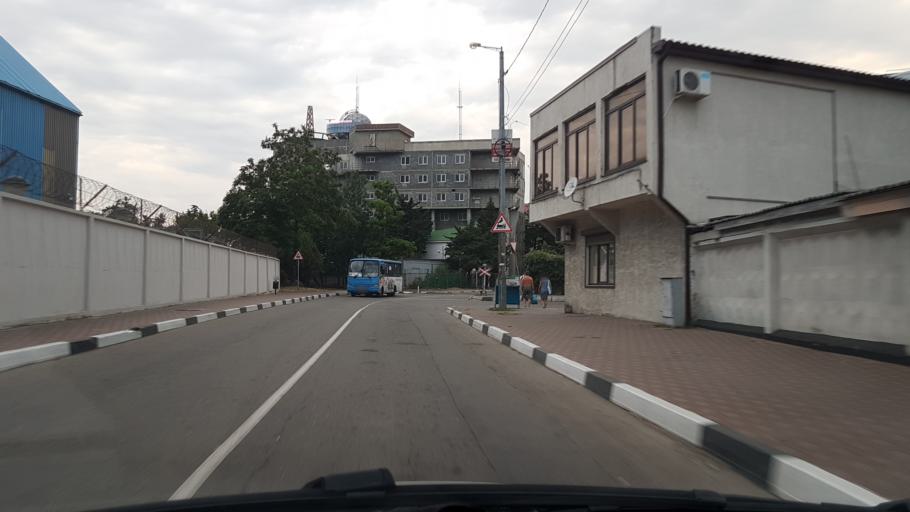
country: RU
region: Krasnodarskiy
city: Tuapse
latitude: 44.0941
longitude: 39.0775
